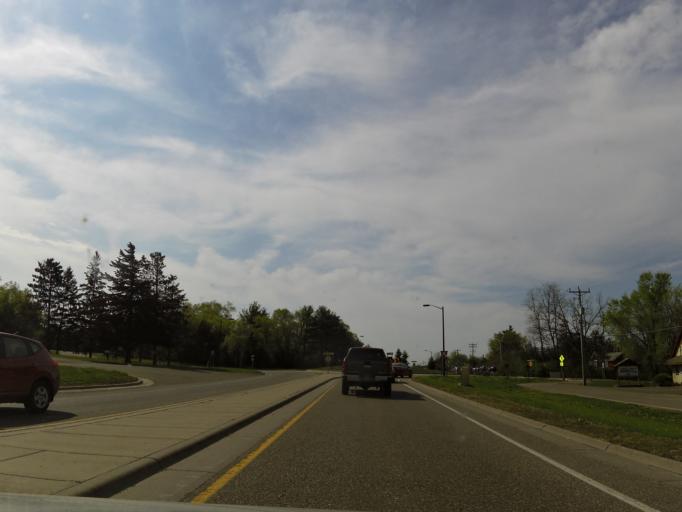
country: US
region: Minnesota
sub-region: Washington County
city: Lakeland
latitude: 44.9503
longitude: -92.7710
